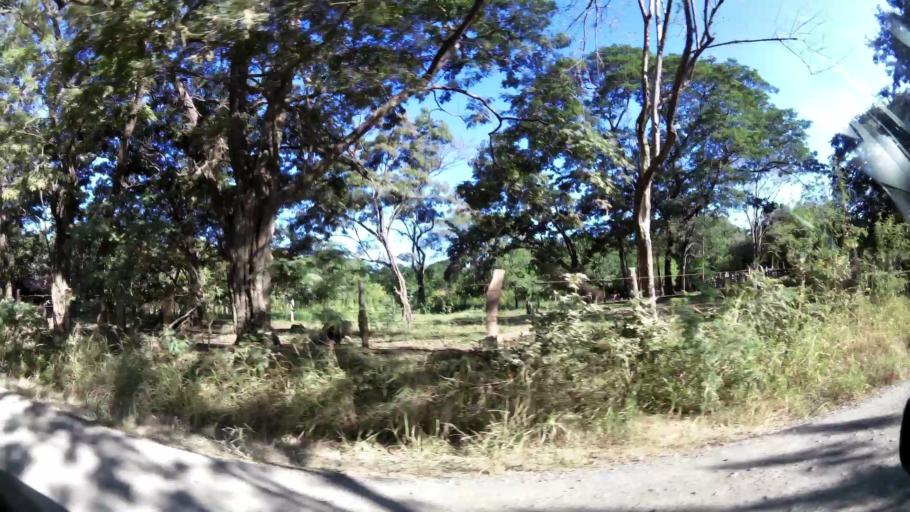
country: CR
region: Guanacaste
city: Sardinal
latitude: 10.4805
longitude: -85.6092
